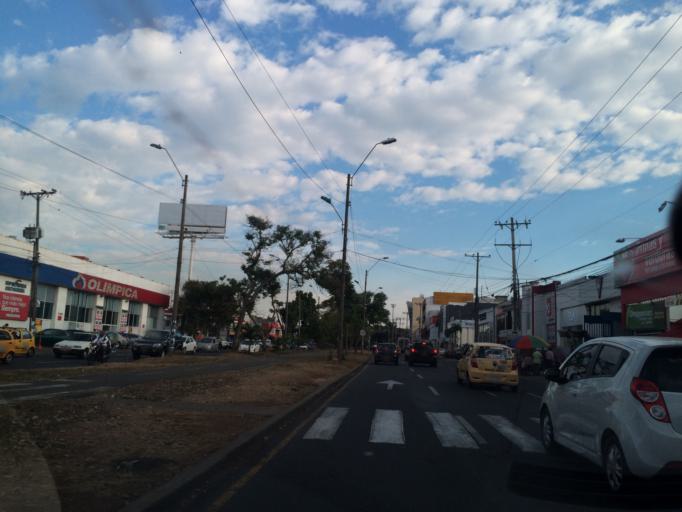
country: CO
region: Valle del Cauca
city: Cali
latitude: 3.3896
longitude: -76.5386
